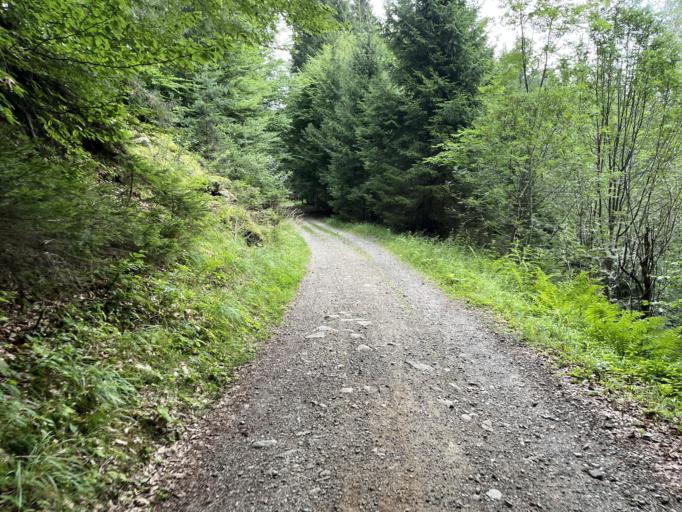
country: AT
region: Carinthia
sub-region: Politischer Bezirk Spittal an der Drau
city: Seeboden
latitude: 46.8011
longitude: 13.5392
